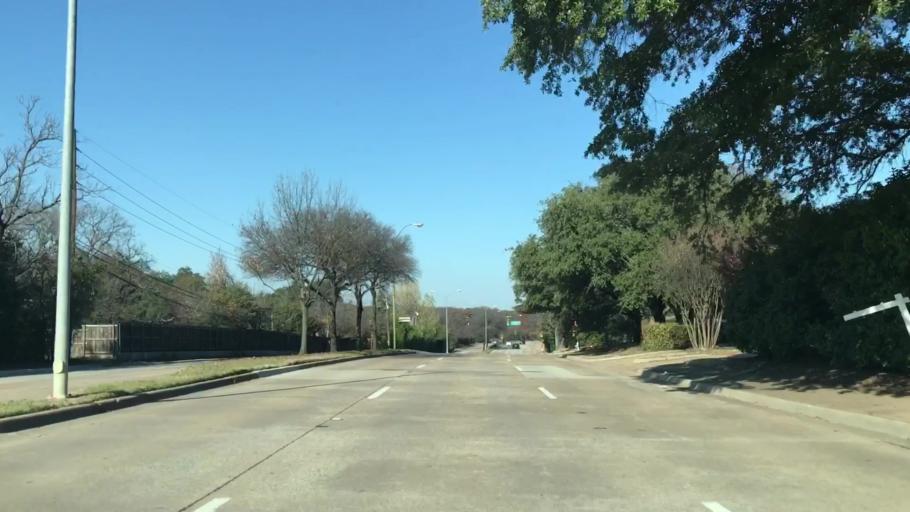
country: US
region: Texas
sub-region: Dallas County
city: University Park
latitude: 32.9002
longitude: -96.7882
